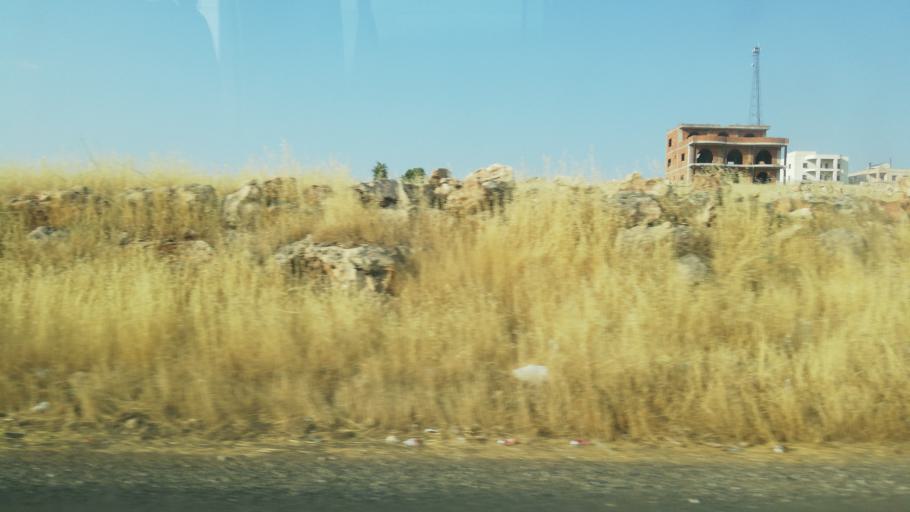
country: TR
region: Mardin
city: Acirli
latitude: 37.4422
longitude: 41.2894
